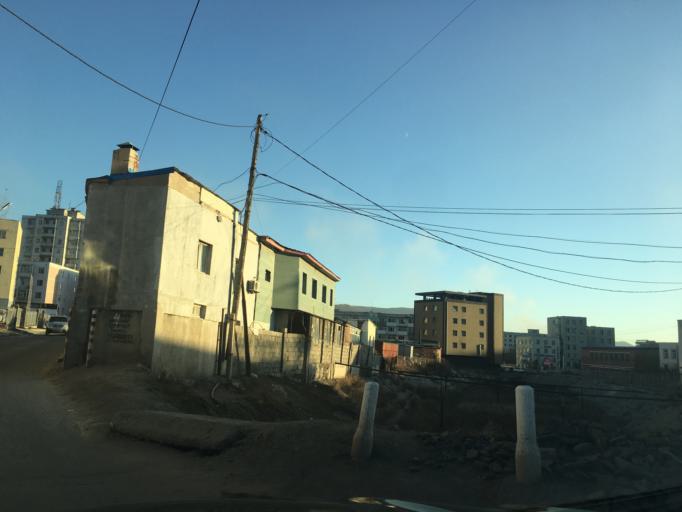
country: MN
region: Ulaanbaatar
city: Ulaanbaatar
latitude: 47.9279
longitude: 106.8860
